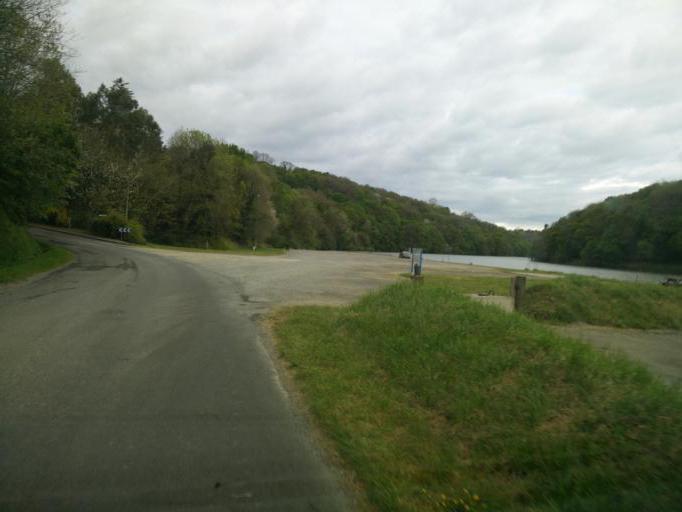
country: FR
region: Brittany
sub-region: Departement des Cotes-d'Armor
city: Lannion
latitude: 48.7370
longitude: -3.4820
